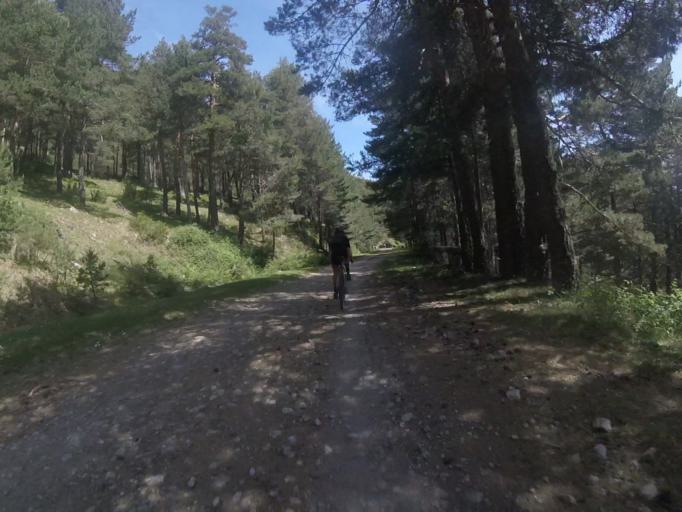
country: ES
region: Madrid
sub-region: Provincia de Madrid
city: Cercedilla
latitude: 40.8026
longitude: -4.0588
